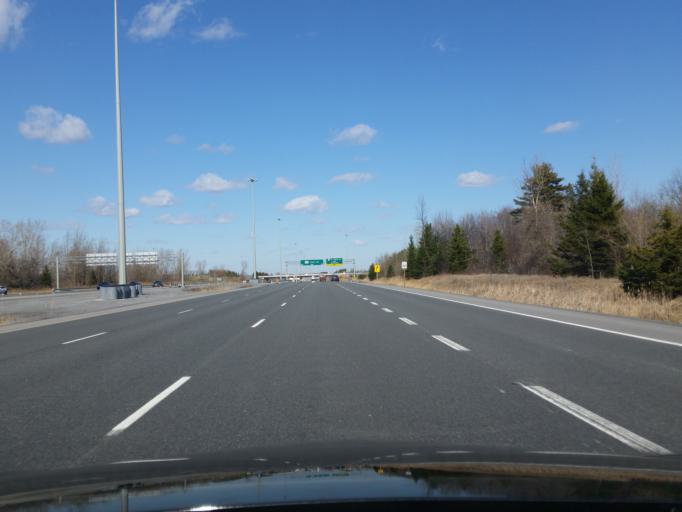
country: CA
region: Ontario
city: Bells Corners
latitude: 45.2764
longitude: -75.9641
